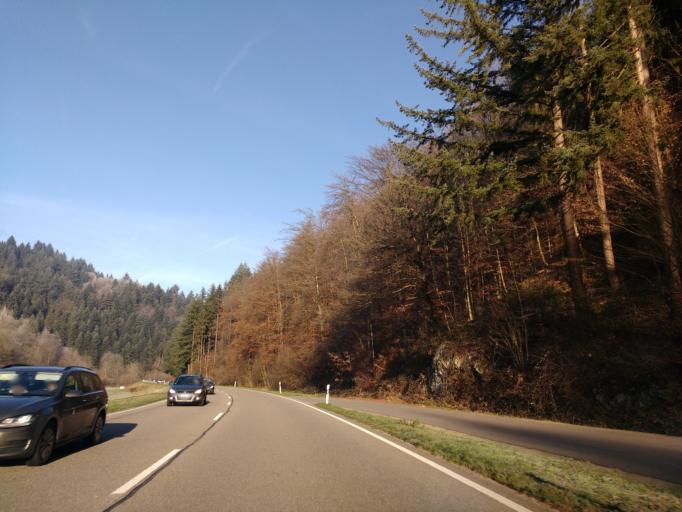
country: DE
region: Baden-Wuerttemberg
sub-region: Freiburg Region
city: Oppenau
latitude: 48.5002
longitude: 8.1391
